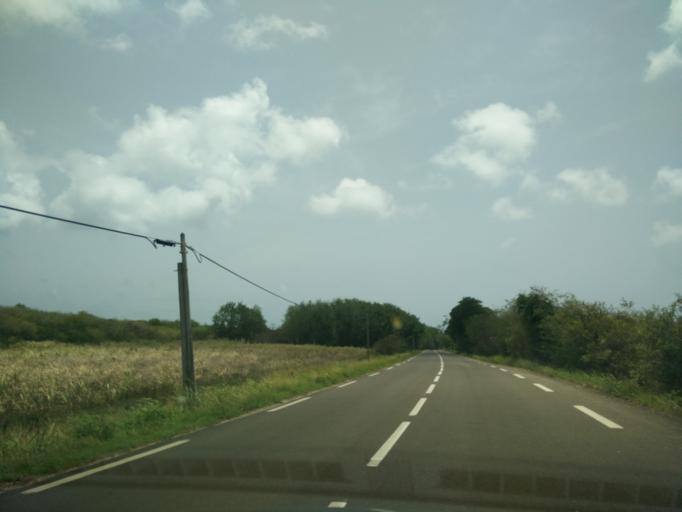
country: GP
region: Guadeloupe
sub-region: Guadeloupe
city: Anse-Bertrand
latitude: 16.4580
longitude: -61.5116
